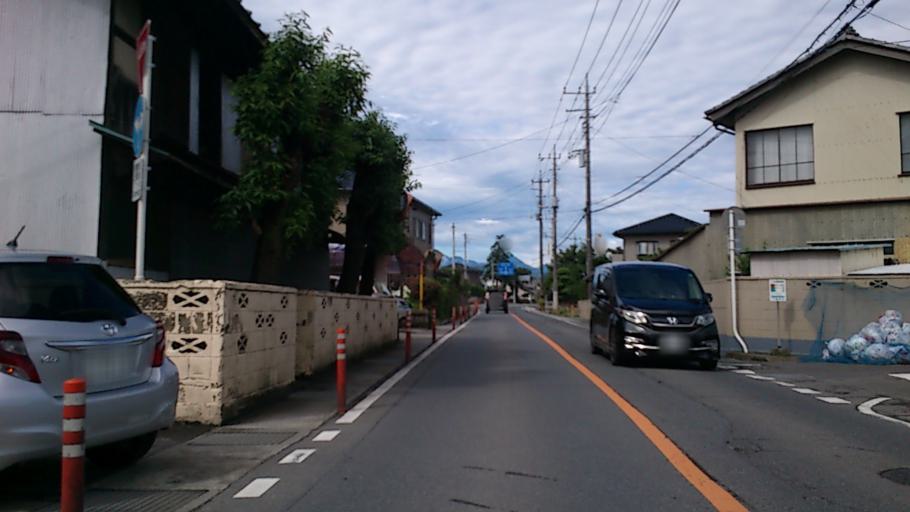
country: JP
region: Gunma
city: Fujioka
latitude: 36.2604
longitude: 139.0908
